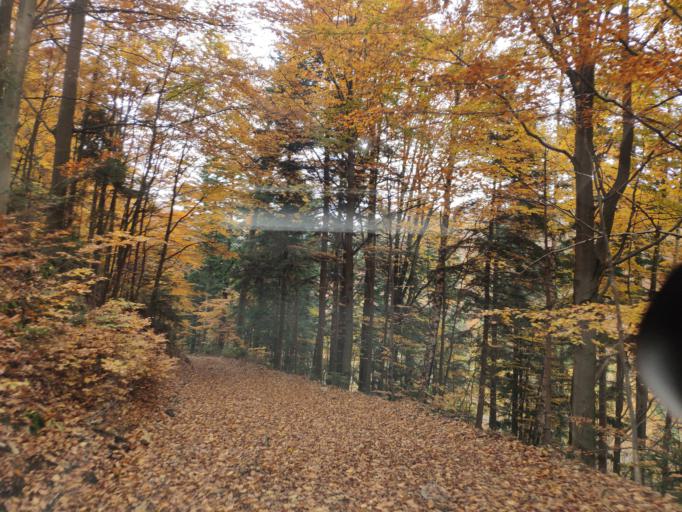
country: SK
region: Kosicky
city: Medzev
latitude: 48.7601
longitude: 20.9751
